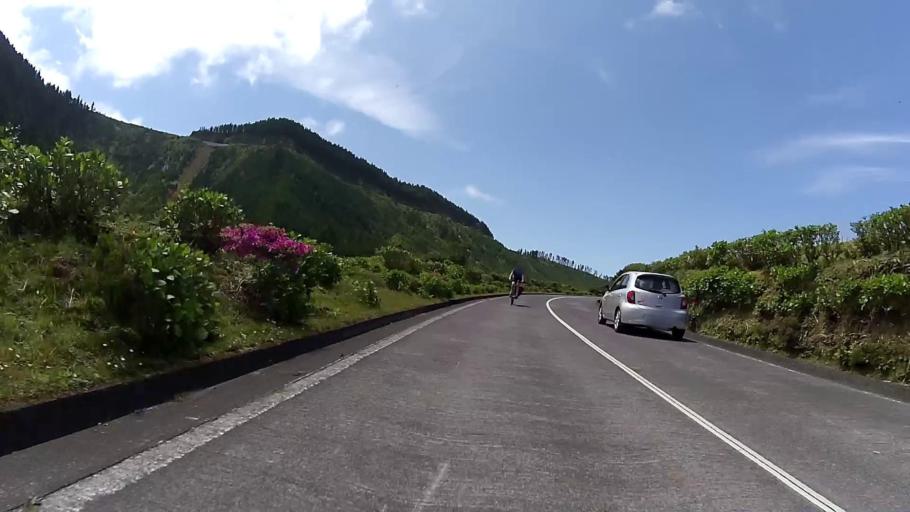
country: PT
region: Azores
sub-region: Ponta Delgada
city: Arrifes
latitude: 37.8428
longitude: -25.7730
